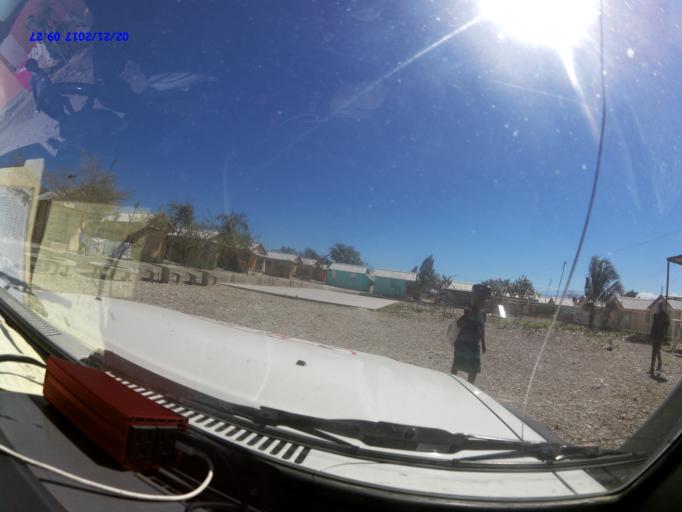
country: HT
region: Ouest
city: Croix des Bouquets
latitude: 18.6551
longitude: -72.2513
